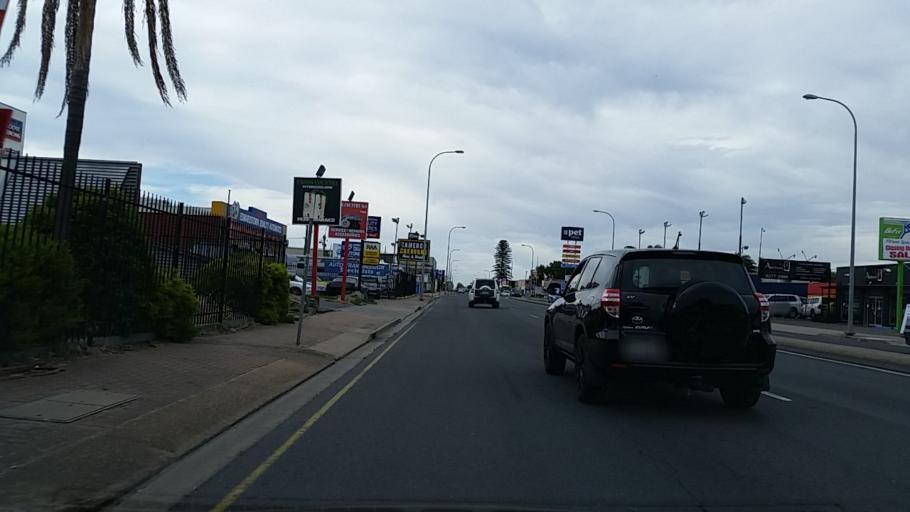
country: AU
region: South Australia
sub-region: Marion
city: Clovelly Park
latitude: -34.9919
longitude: 138.5747
